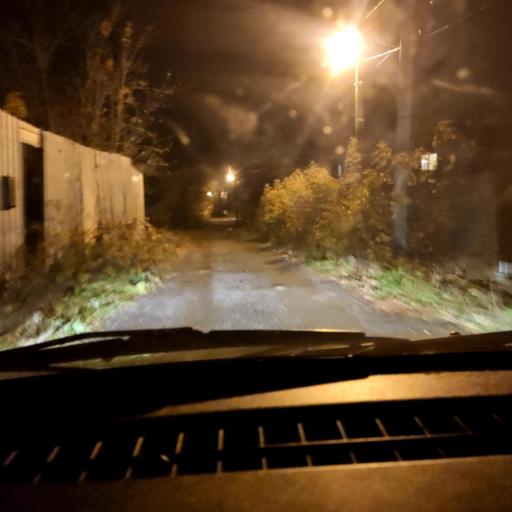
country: RU
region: Bashkortostan
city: Ufa
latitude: 54.7014
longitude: 55.9436
